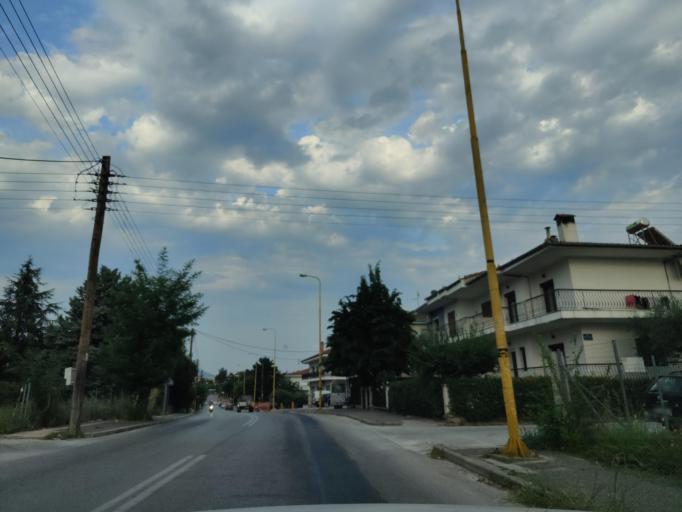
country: GR
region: East Macedonia and Thrace
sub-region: Nomos Dramas
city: Drama
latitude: 41.1529
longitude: 24.1282
